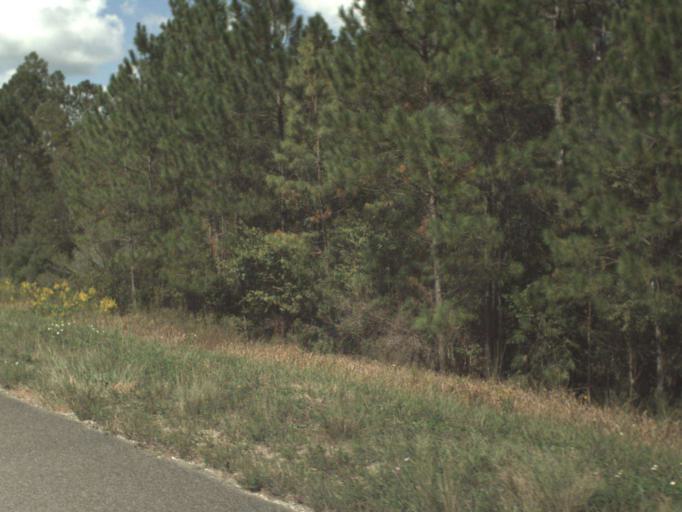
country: US
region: Florida
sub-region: Bay County
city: Laguna Beach
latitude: 30.4534
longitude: -85.9053
